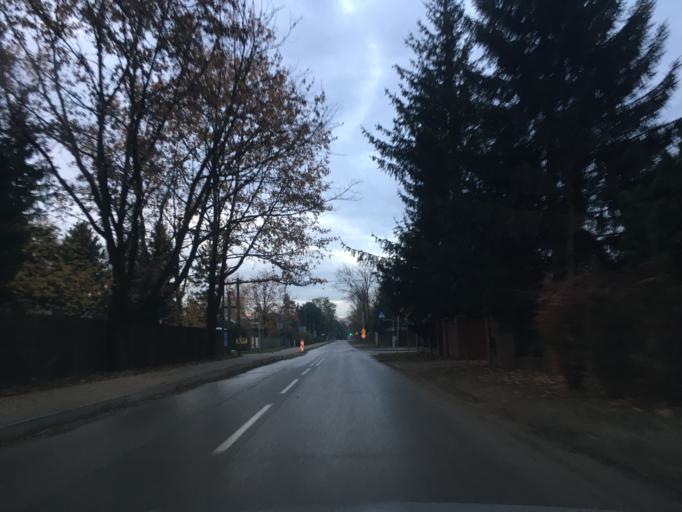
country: PL
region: Masovian Voivodeship
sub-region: Powiat piaseczynski
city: Piaseczno
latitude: 52.0581
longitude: 20.9815
